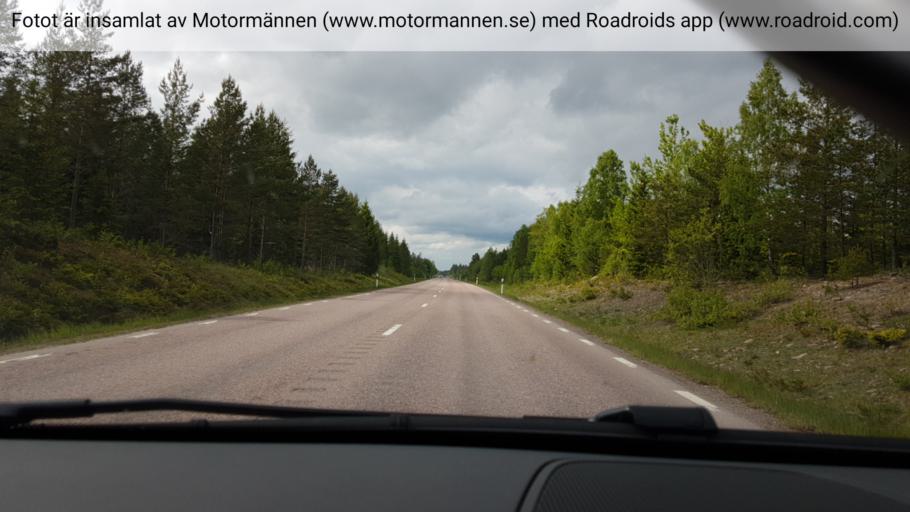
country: SE
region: Uppsala
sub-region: Tierps Kommun
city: Tierp
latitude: 60.2966
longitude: 17.5747
